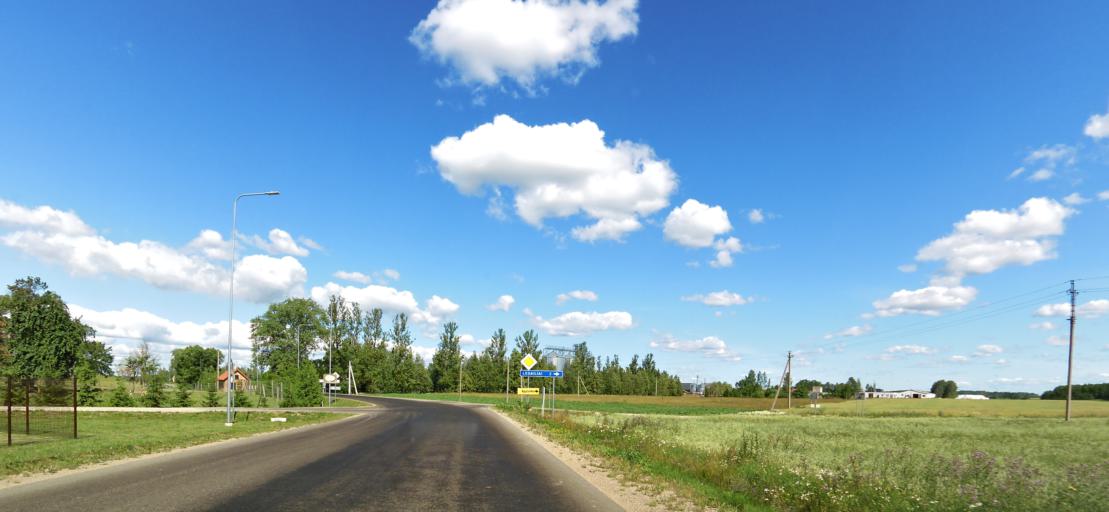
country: LT
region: Panevezys
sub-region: Birzai
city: Birzai
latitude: 56.2894
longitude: 24.6443
